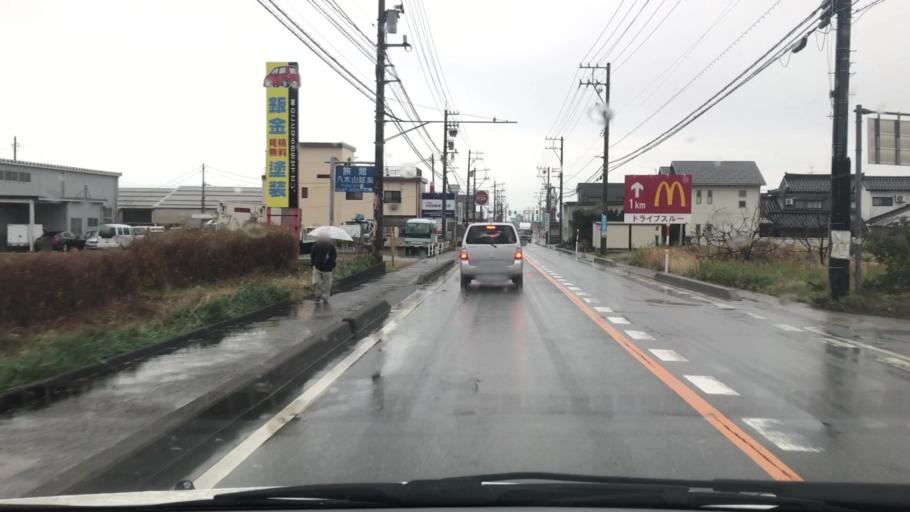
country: JP
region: Toyama
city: Yatsuomachi-higashikumisaka
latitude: 36.5855
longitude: 137.2060
